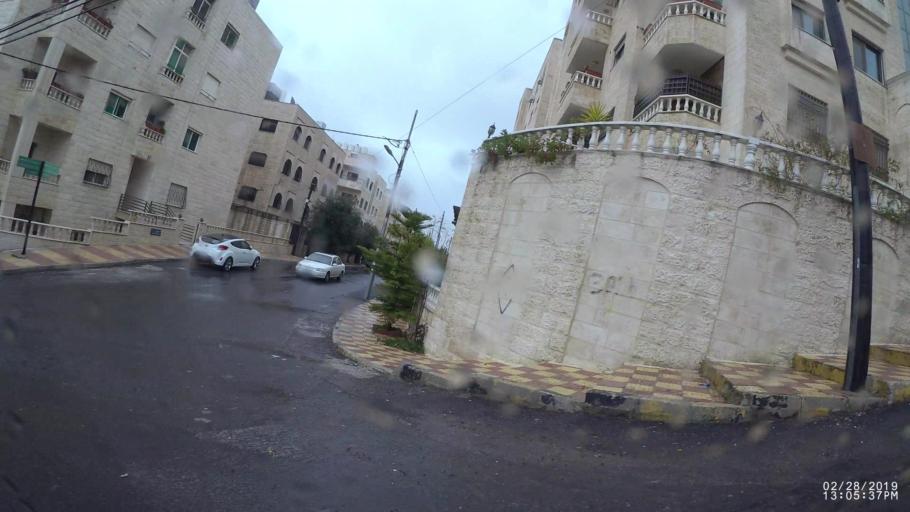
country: JO
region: Amman
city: Al Jubayhah
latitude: 32.0218
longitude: 35.8809
